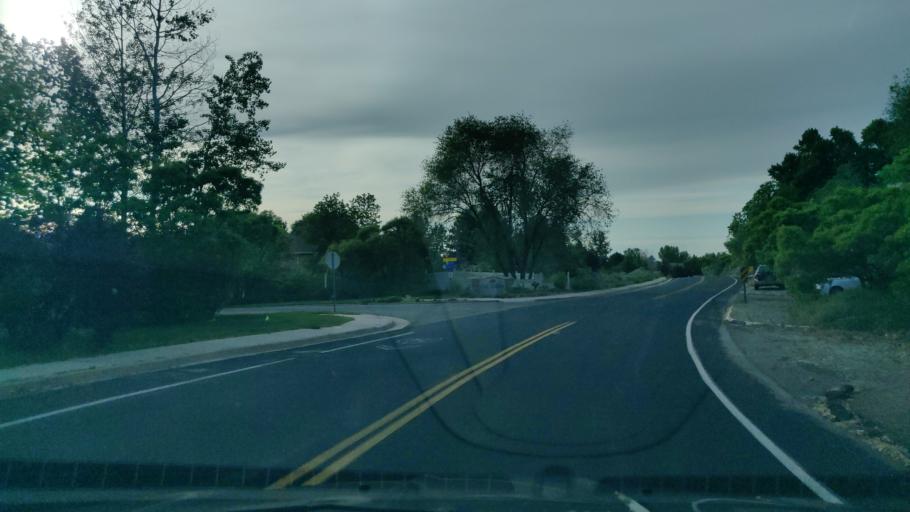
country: US
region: Utah
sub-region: Salt Lake County
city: Granite
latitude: 40.5897
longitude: -111.7985
